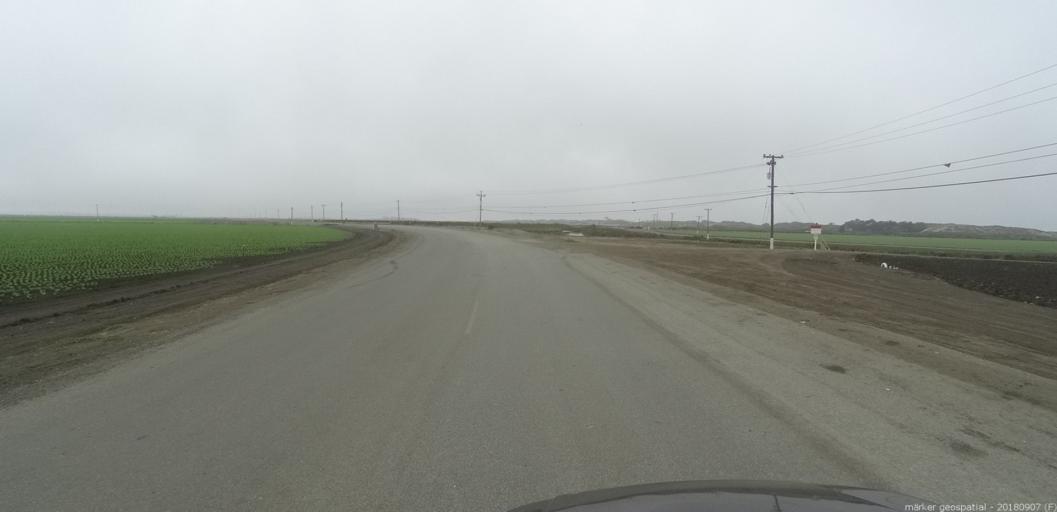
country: US
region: California
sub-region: Monterey County
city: Castroville
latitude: 36.7735
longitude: -121.7865
